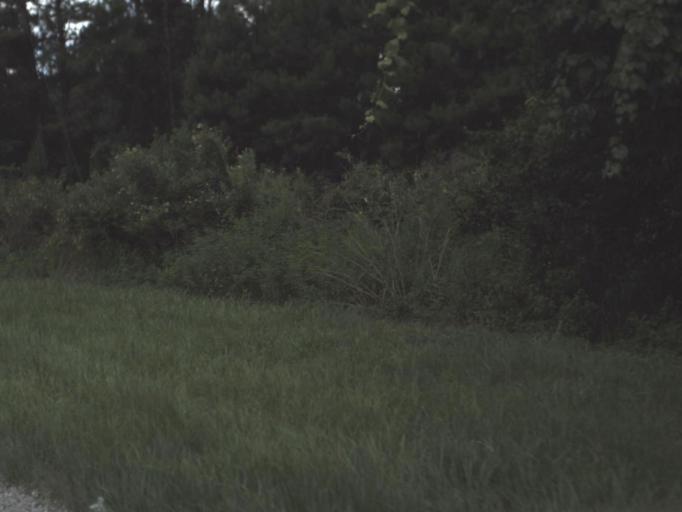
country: US
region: Florida
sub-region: Clay County
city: Keystone Heights
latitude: 29.6832
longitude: -82.0353
